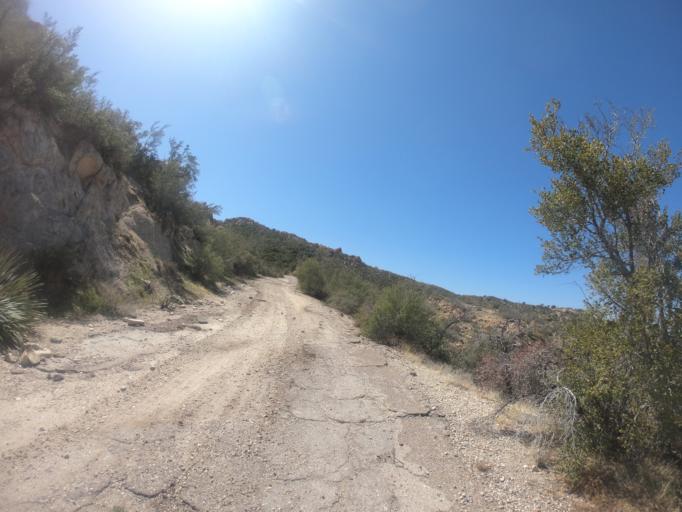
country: US
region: Arizona
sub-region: Gila County
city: Miami
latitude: 33.3587
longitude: -110.9539
